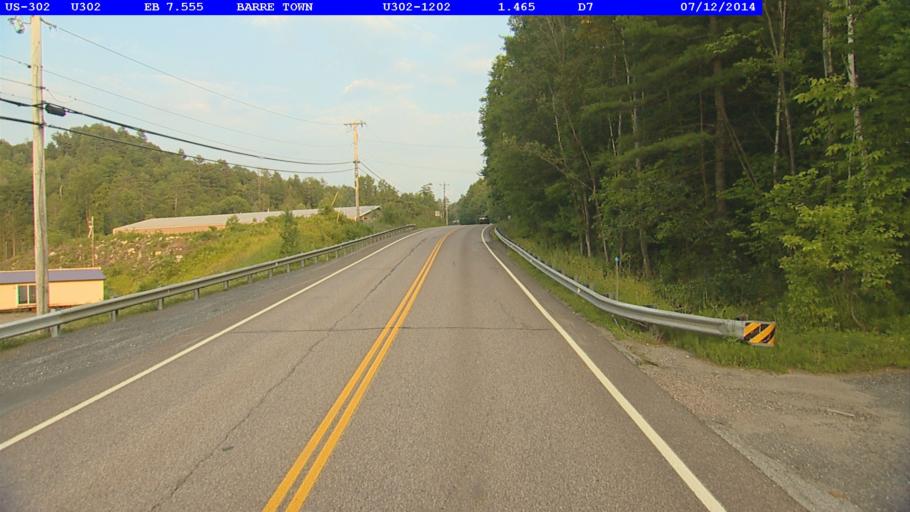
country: US
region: Vermont
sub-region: Washington County
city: South Barre
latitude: 44.1712
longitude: -72.4640
